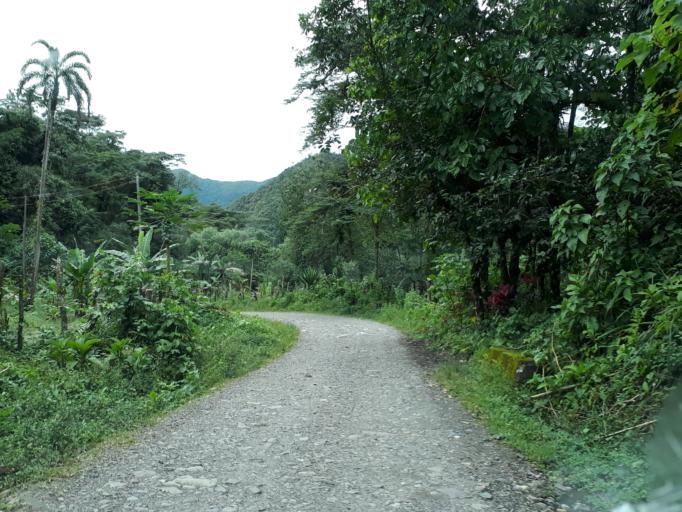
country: CO
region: Boyaca
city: Santa Maria
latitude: 4.7524
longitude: -73.3244
